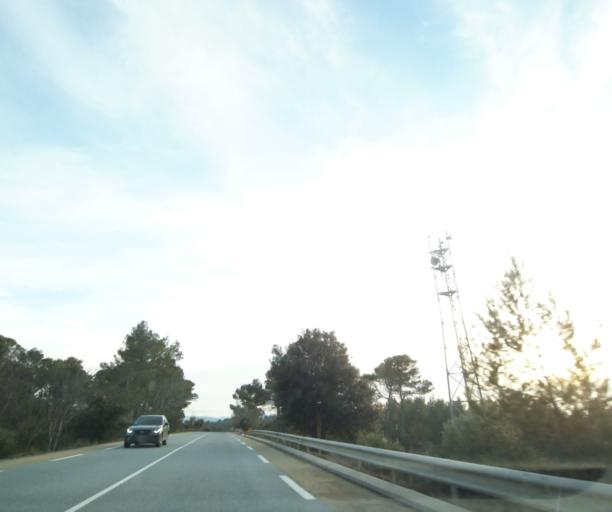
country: FR
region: Provence-Alpes-Cote d'Azur
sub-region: Departement du Var
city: La Motte
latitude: 43.5130
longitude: 6.5169
